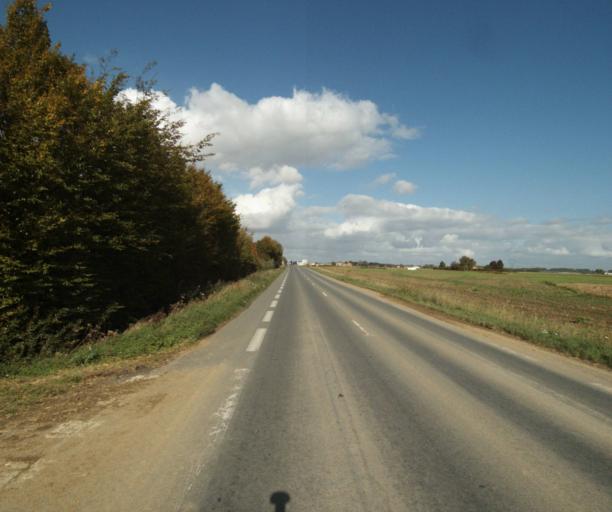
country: FR
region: Nord-Pas-de-Calais
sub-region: Departement du Nord
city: Frelinghien
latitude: 50.7082
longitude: 2.9376
